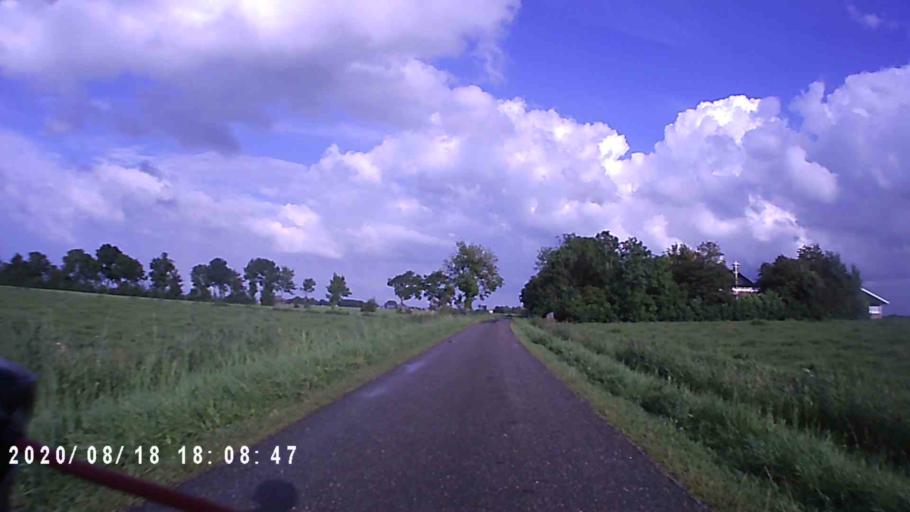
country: NL
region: Groningen
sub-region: Gemeente Zuidhorn
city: Noordhorn
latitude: 53.2822
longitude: 6.3977
